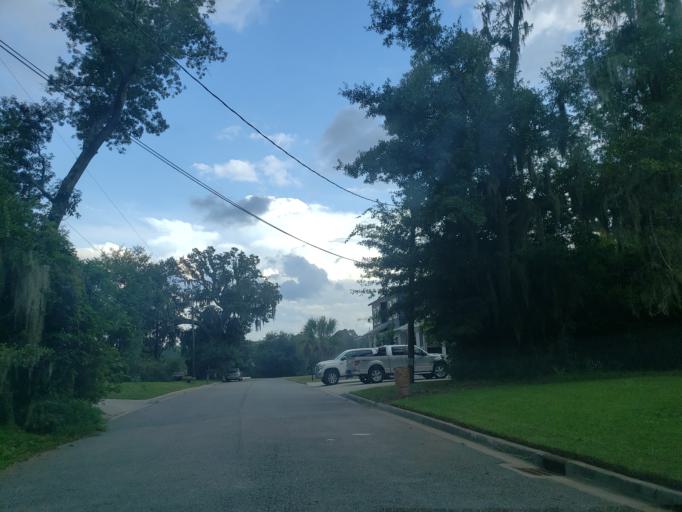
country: US
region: Georgia
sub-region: Chatham County
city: Isle of Hope
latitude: 31.9877
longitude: -81.0700
